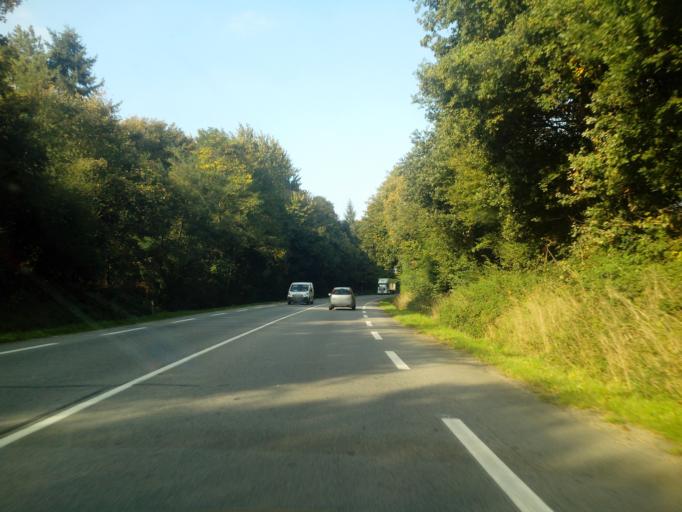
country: FR
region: Brittany
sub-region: Departement du Morbihan
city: Ploermel
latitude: 47.9240
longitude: -2.3859
